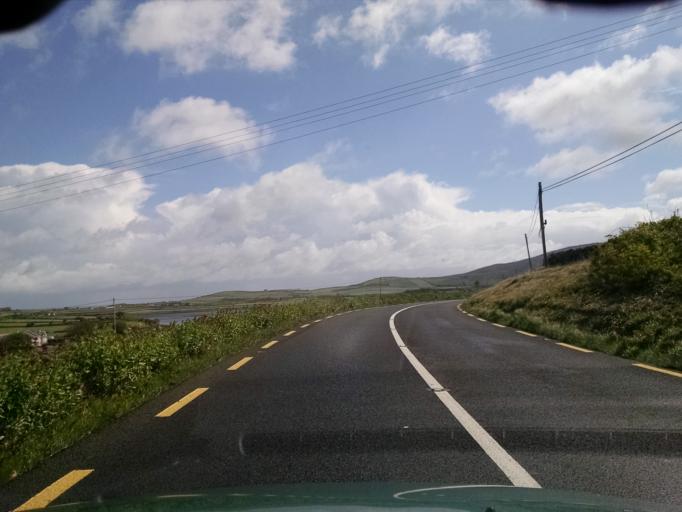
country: IE
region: Connaught
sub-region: County Galway
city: Bearna
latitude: 53.1364
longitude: -9.1052
